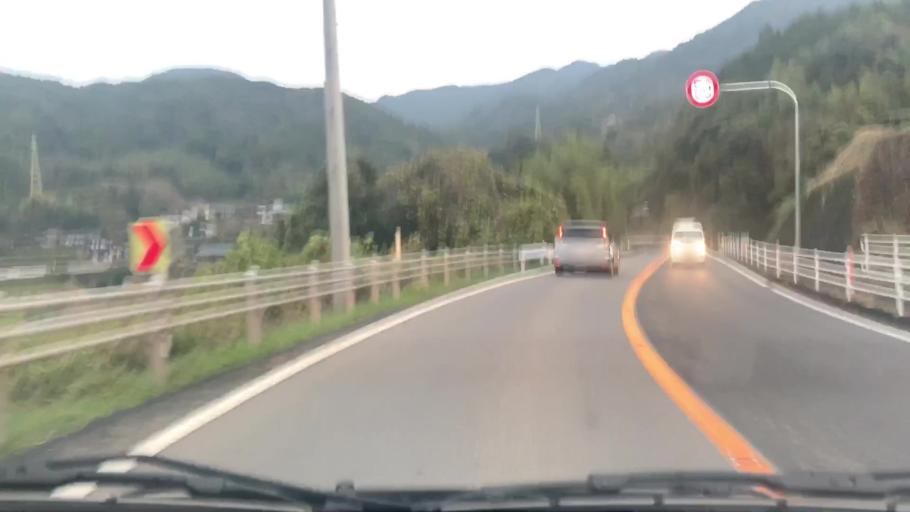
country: JP
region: Saga Prefecture
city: Ureshinomachi-shimojuku
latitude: 33.0532
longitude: 129.9372
